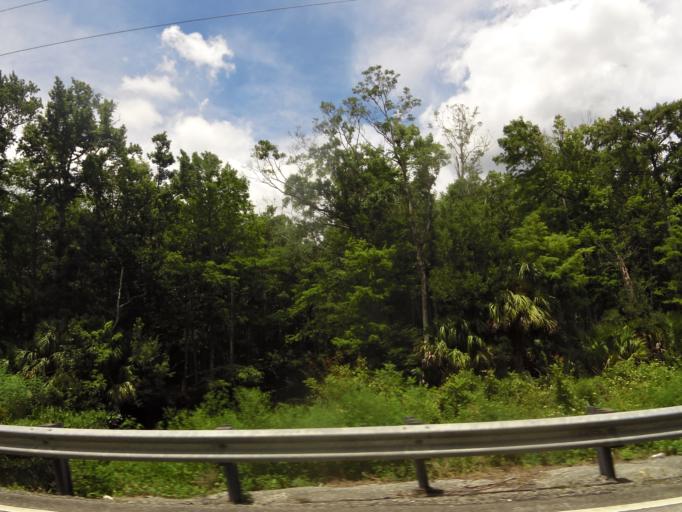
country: US
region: Florida
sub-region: Flagler County
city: Palm Coast
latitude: 29.6587
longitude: -81.2902
